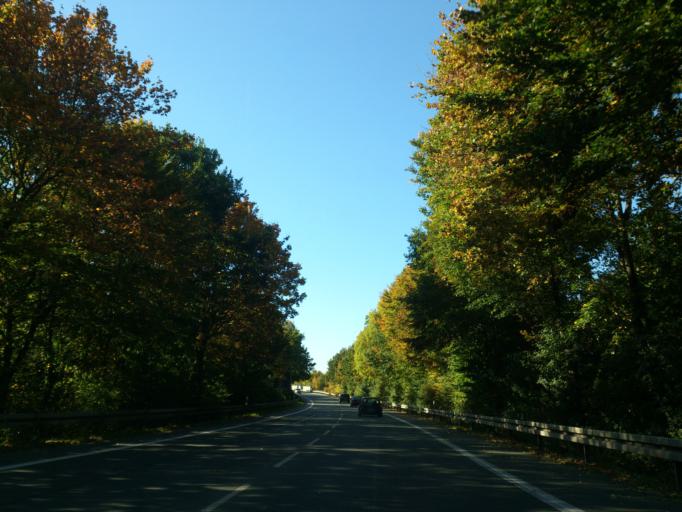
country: DE
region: North Rhine-Westphalia
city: Warburg
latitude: 51.4925
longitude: 9.1445
